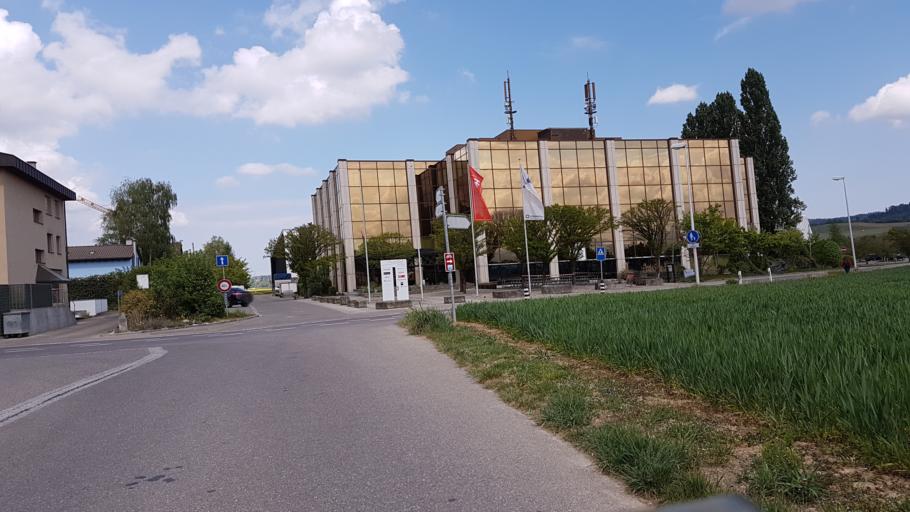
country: CH
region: Bern
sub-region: Bern-Mittelland District
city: Belp
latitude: 46.9008
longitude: 7.5050
